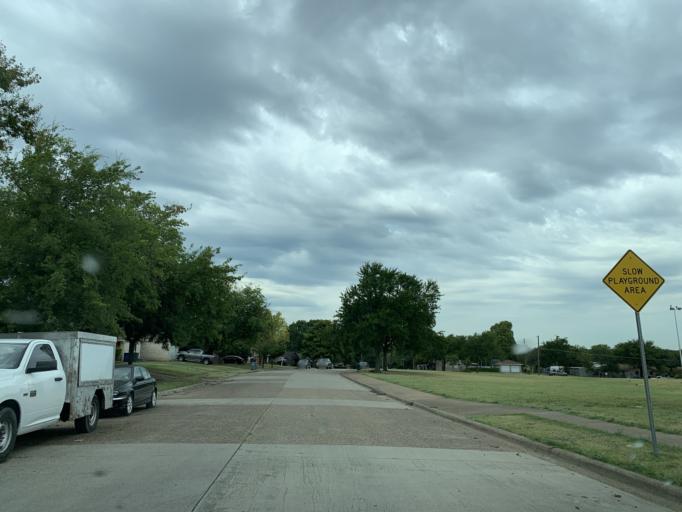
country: US
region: Texas
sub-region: Dallas County
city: Duncanville
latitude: 32.6645
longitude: -96.8310
